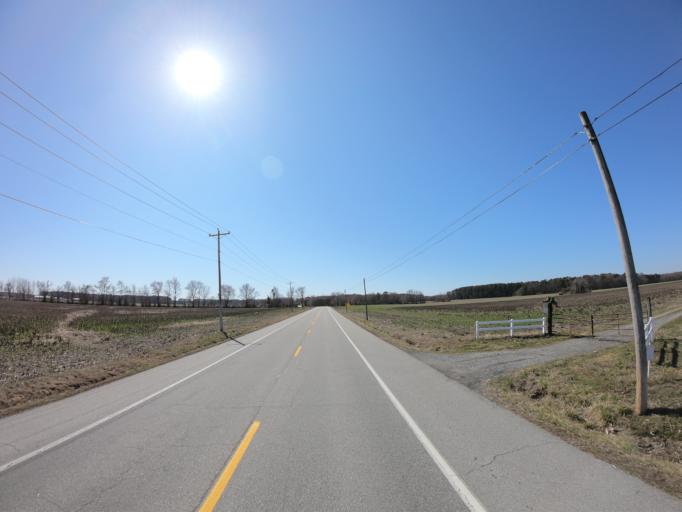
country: US
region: Maryland
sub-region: Kent County
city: Rock Hall
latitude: 39.1630
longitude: -76.2033
